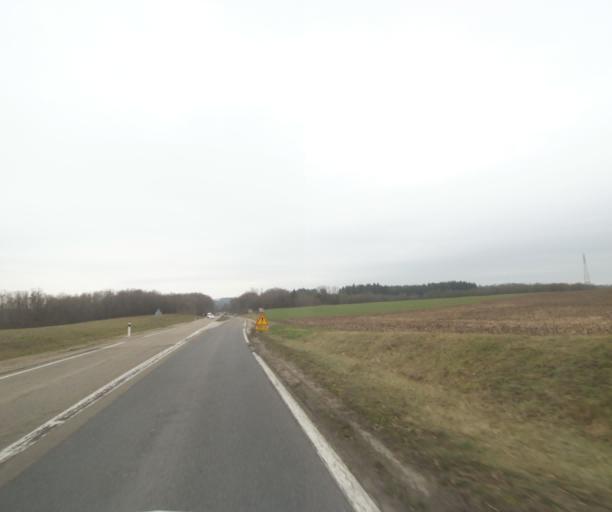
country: FR
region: Champagne-Ardenne
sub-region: Departement de la Haute-Marne
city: Bienville
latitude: 48.5746
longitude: 5.0354
